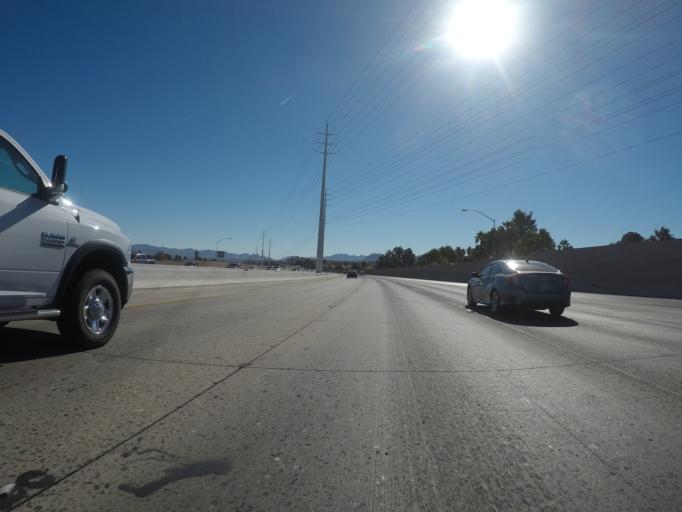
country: US
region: Nevada
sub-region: Clark County
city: Whitney
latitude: 36.0972
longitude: -115.0802
